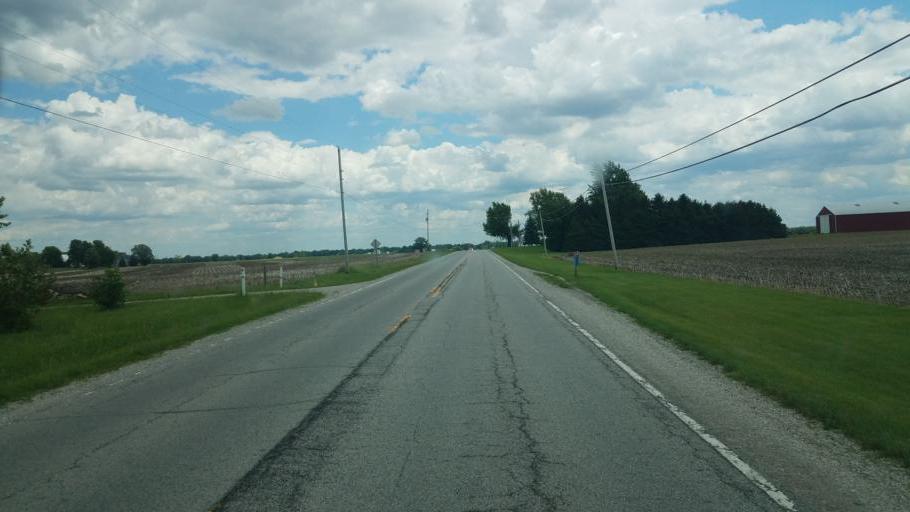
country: US
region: Ohio
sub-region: Crawford County
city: Bucyrus
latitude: 40.8184
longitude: -83.0141
